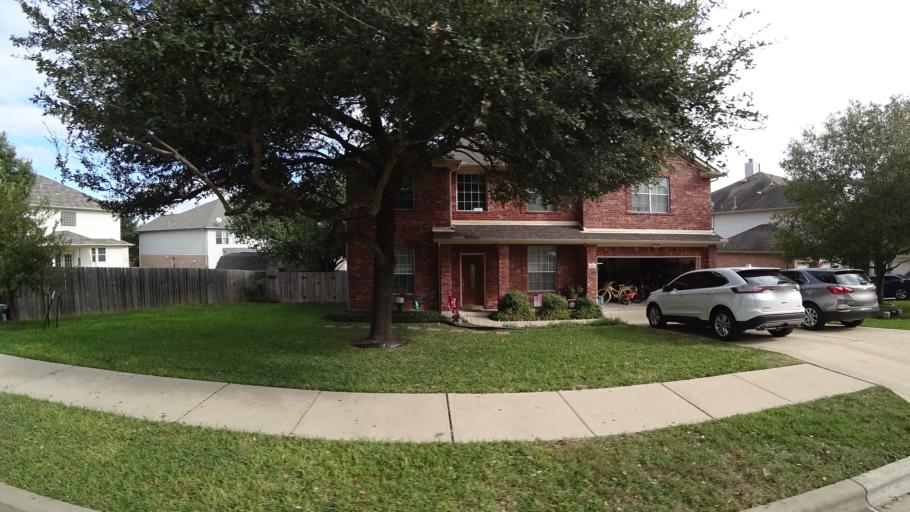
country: US
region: Texas
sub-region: Travis County
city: Pflugerville
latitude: 30.4297
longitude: -97.6271
